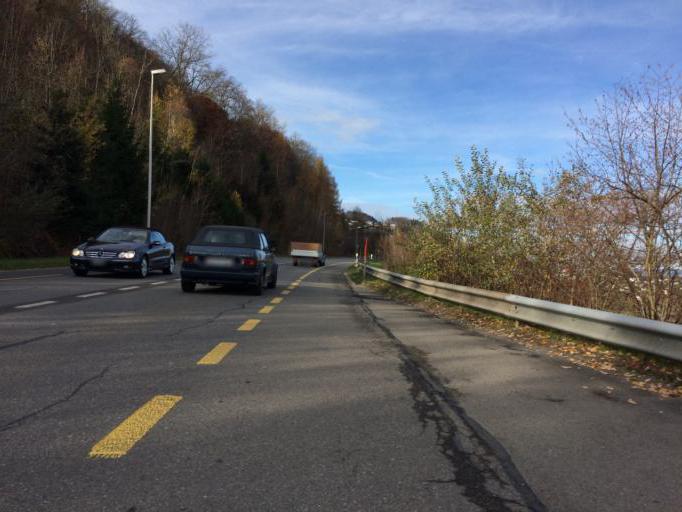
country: CH
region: Bern
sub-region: Bern-Mittelland District
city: Kehrsatz
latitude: 46.9041
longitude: 7.4807
